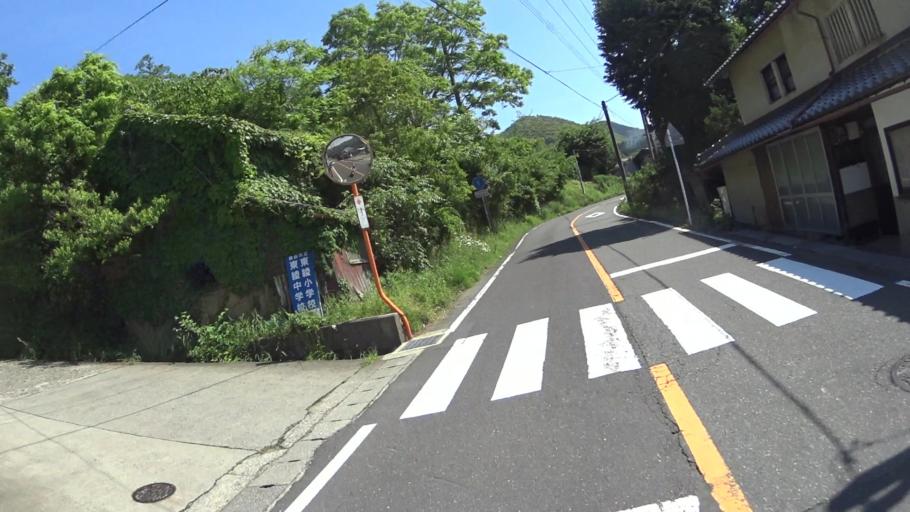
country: JP
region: Kyoto
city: Ayabe
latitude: 35.2962
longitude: 135.3157
